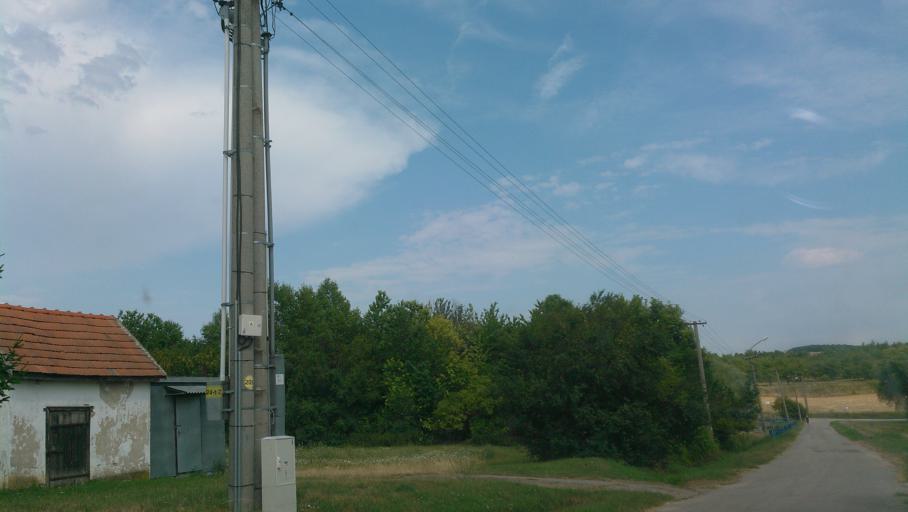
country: SK
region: Nitriansky
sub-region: Okres Nitra
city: Nitra
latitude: 48.5061
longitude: 18.0612
